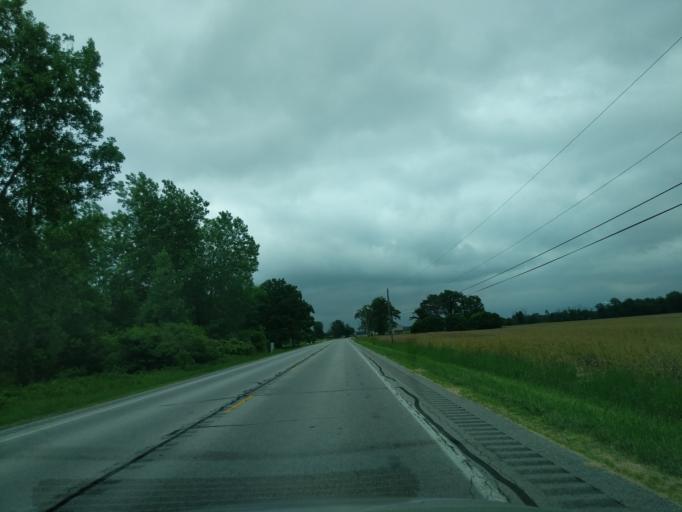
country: US
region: Indiana
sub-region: Madison County
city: Frankton
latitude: 40.2775
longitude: -85.7411
